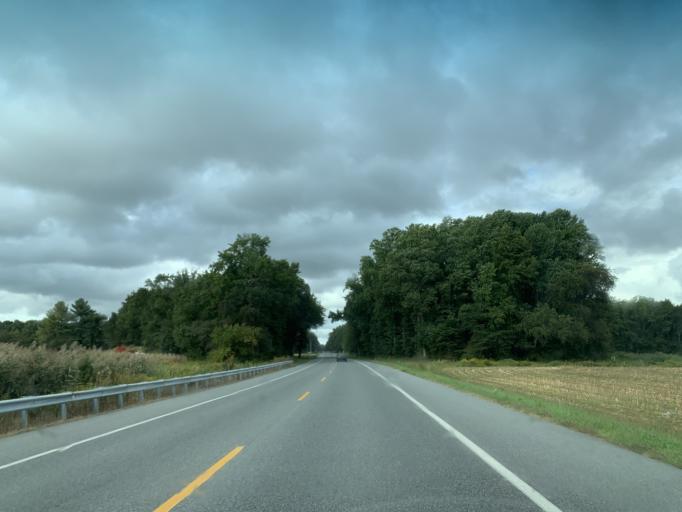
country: US
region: Maryland
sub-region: Caroline County
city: Ridgely
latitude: 39.0077
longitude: -75.8731
